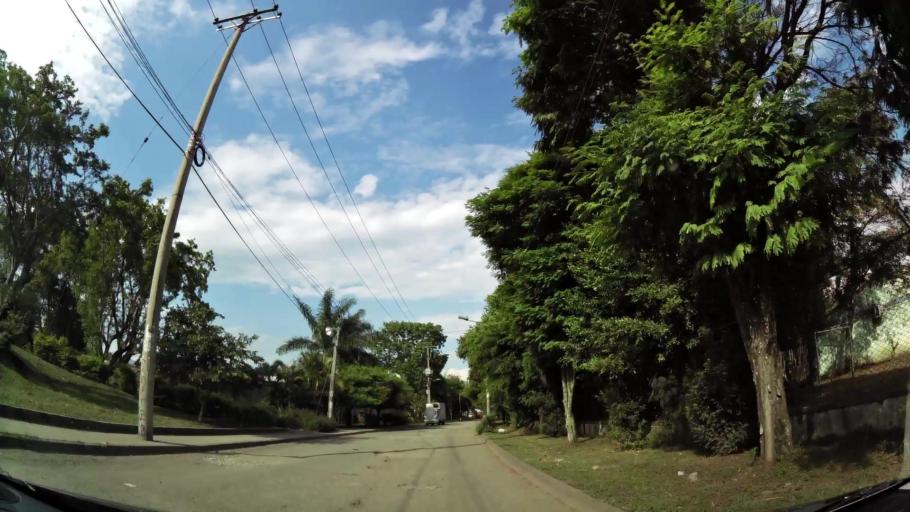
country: CO
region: Valle del Cauca
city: Cali
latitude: 3.4668
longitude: -76.5177
